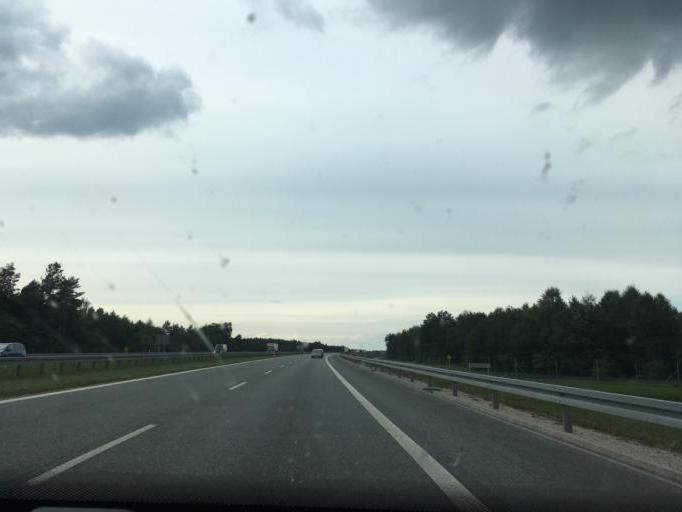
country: PL
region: Lodz Voivodeship
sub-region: Powiat zdunskowolski
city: Zdunska Wola
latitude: 51.5825
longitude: 18.9049
